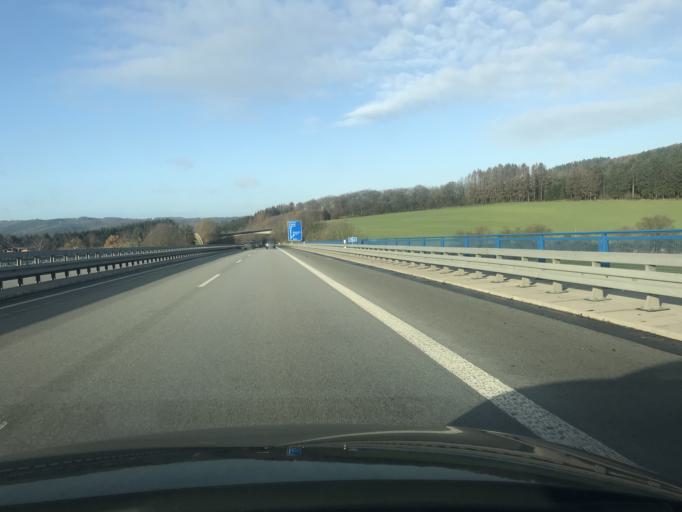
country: DE
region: North Rhine-Westphalia
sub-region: Regierungsbezirk Arnsberg
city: Meschede
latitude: 51.3585
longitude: 8.2035
